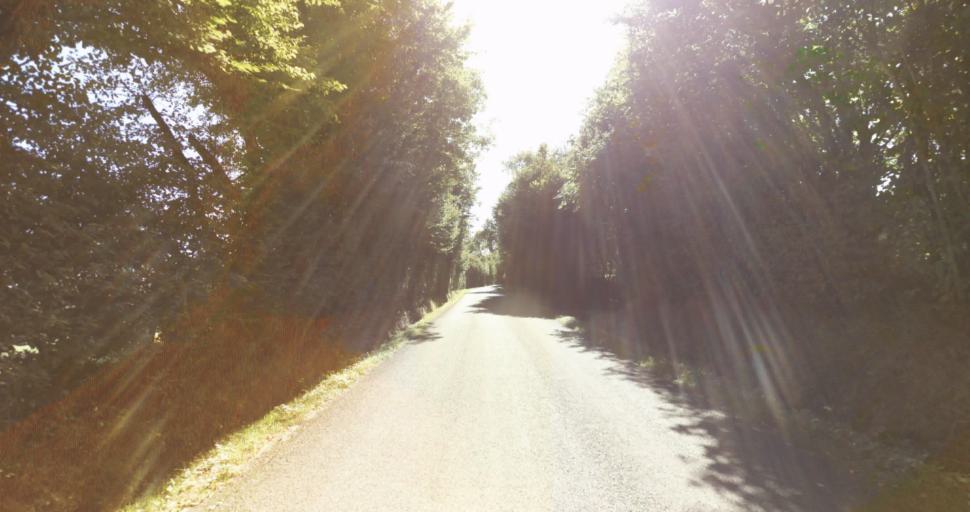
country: FR
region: Lower Normandy
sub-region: Departement de l'Orne
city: Gace
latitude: 48.7655
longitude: 0.2541
